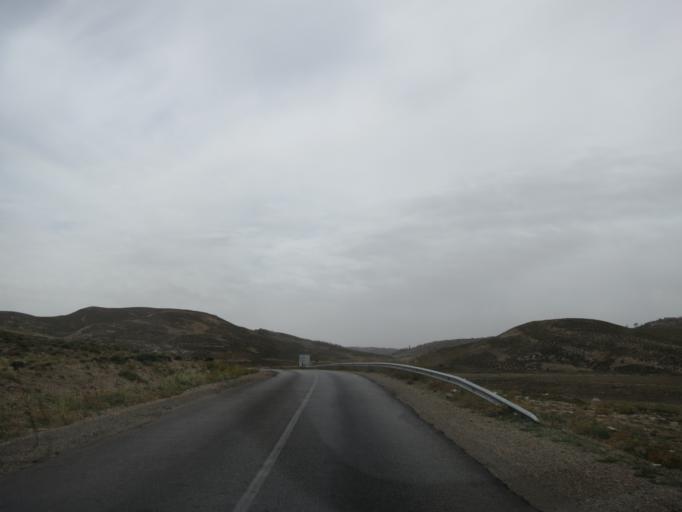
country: MA
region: Meknes-Tafilalet
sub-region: Khenifra
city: Itzer
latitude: 33.1158
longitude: -5.0299
